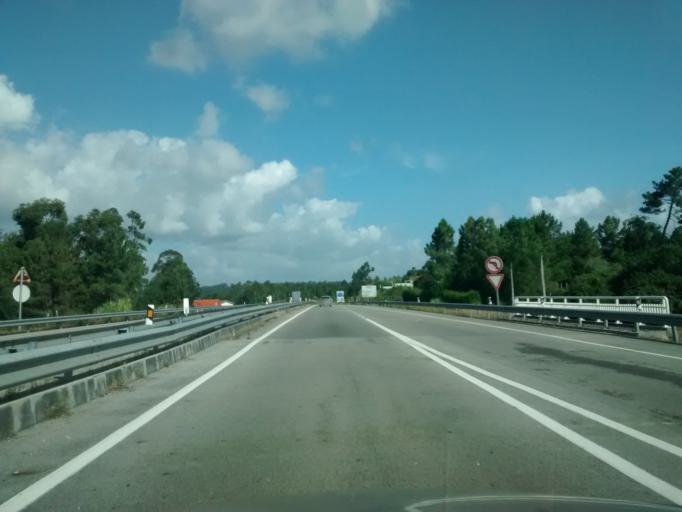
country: PT
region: Aveiro
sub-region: Oliveira do Bairro
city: Oliveira do Bairro
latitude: 40.5155
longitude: -8.5013
